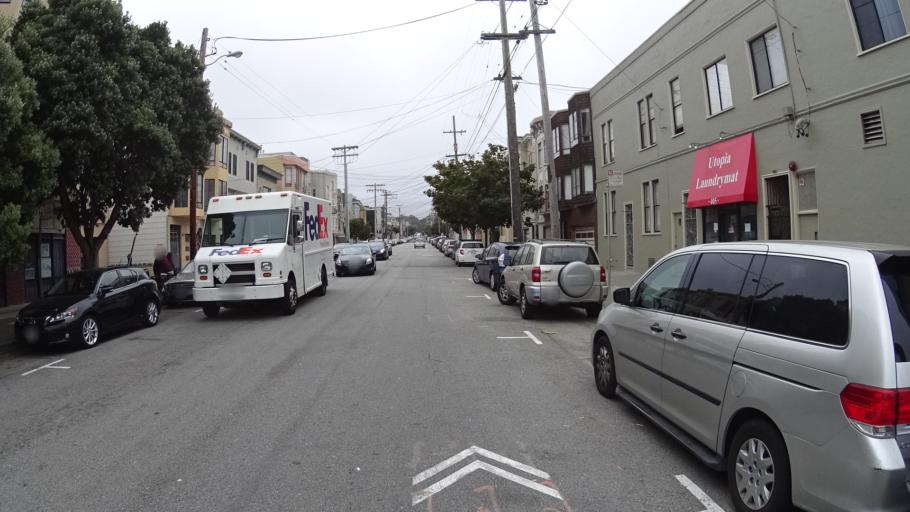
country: US
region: California
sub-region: San Francisco County
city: San Francisco
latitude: 37.7808
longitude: -122.4664
